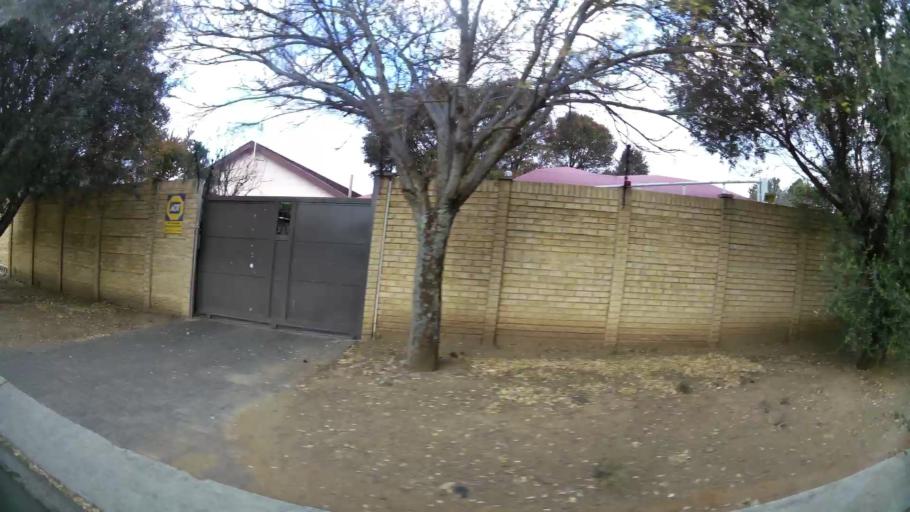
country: ZA
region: Orange Free State
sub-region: Mangaung Metropolitan Municipality
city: Bloemfontein
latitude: -29.0728
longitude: 26.2087
